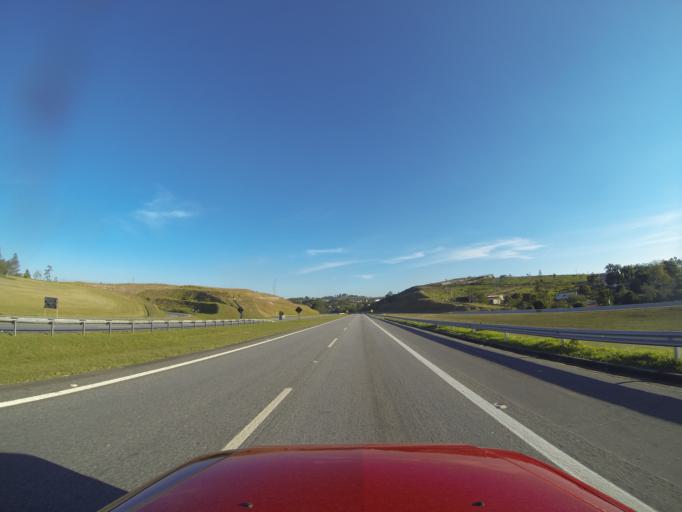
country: BR
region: Sao Paulo
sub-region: Jacarei
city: Jacarei
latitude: -23.3101
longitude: -46.0453
